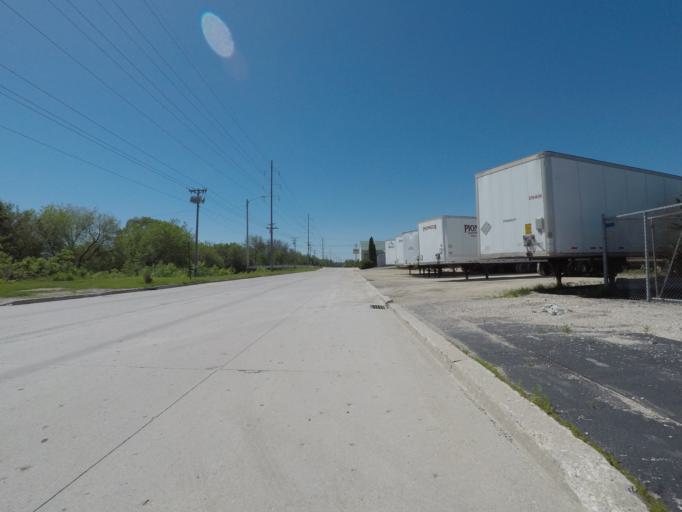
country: US
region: Wisconsin
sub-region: Sheboygan County
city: Sheboygan
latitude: 43.7555
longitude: -87.7296
